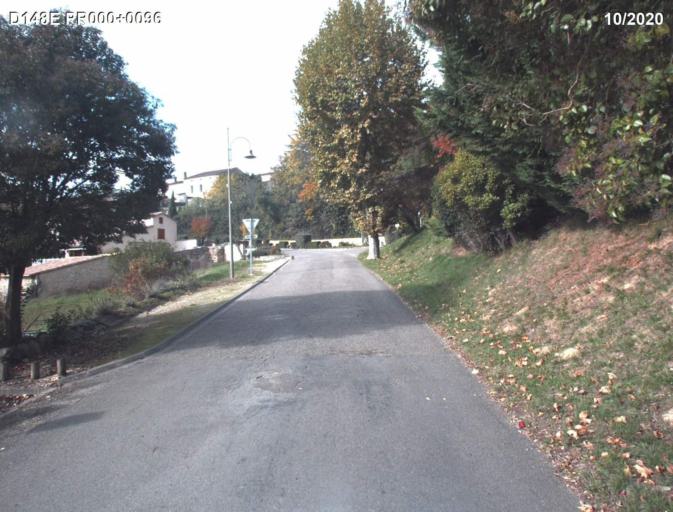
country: FR
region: Aquitaine
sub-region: Departement du Lot-et-Garonne
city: Beaupuy
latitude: 44.5588
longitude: 0.1342
